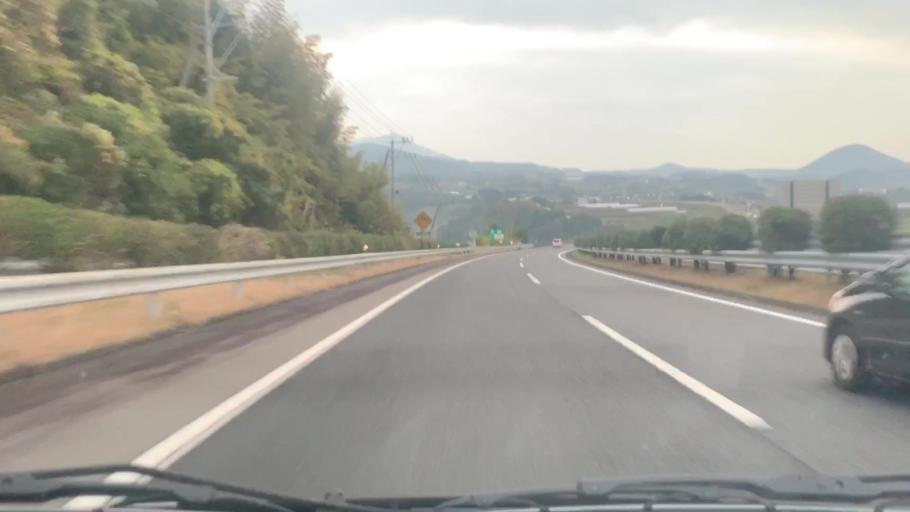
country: JP
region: Nagasaki
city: Omura
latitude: 33.0261
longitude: 129.9387
